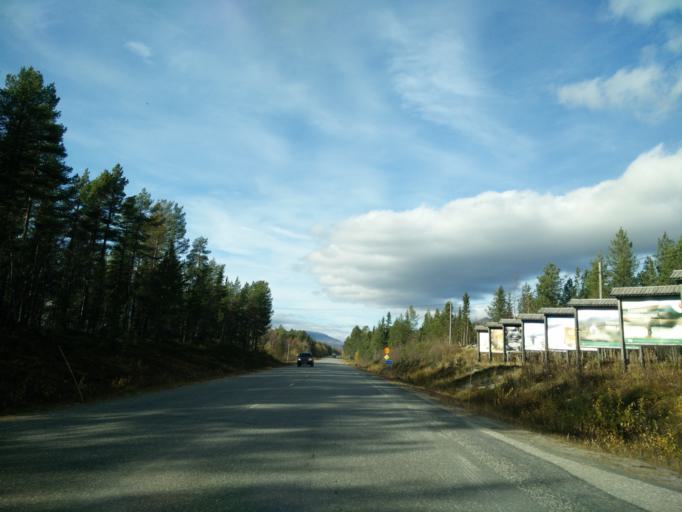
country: NO
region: Hedmark
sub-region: Engerdal
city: Engerdal
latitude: 62.5233
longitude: 12.5885
